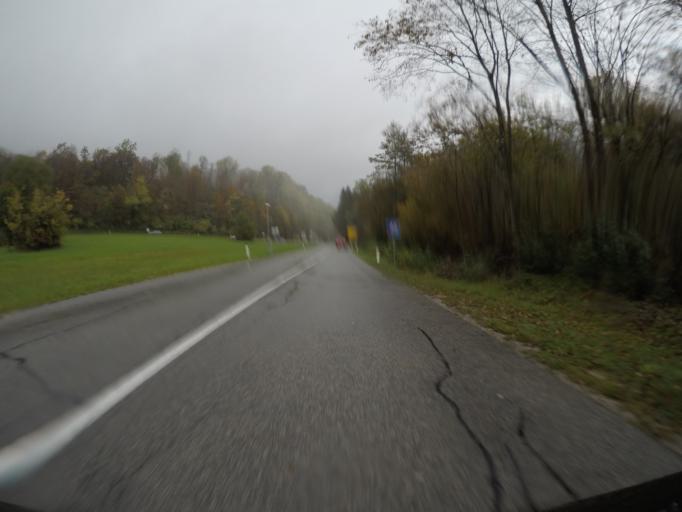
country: SI
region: Bovec
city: Bovec
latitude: 46.3428
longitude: 13.5737
